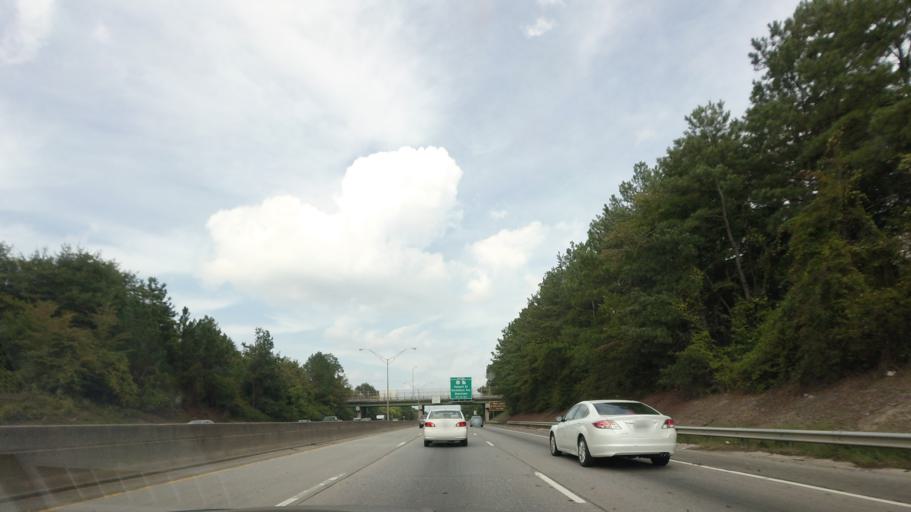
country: US
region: Georgia
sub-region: Bibb County
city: Macon
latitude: 32.8339
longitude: -83.6502
